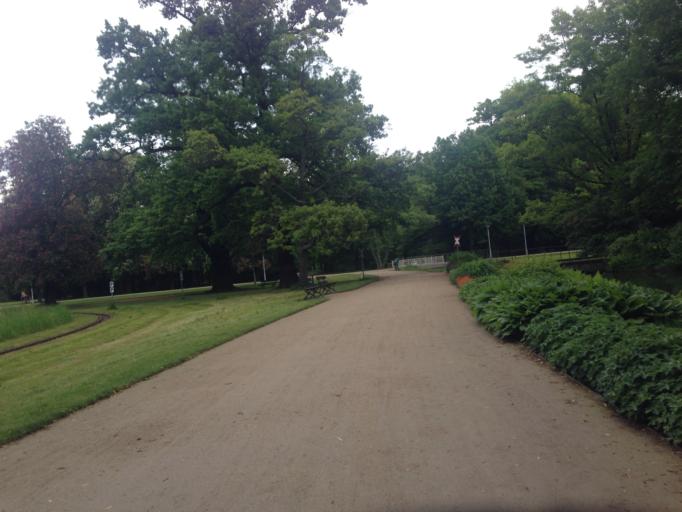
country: DE
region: Saxony
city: Dresden
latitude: 51.0351
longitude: 13.7676
